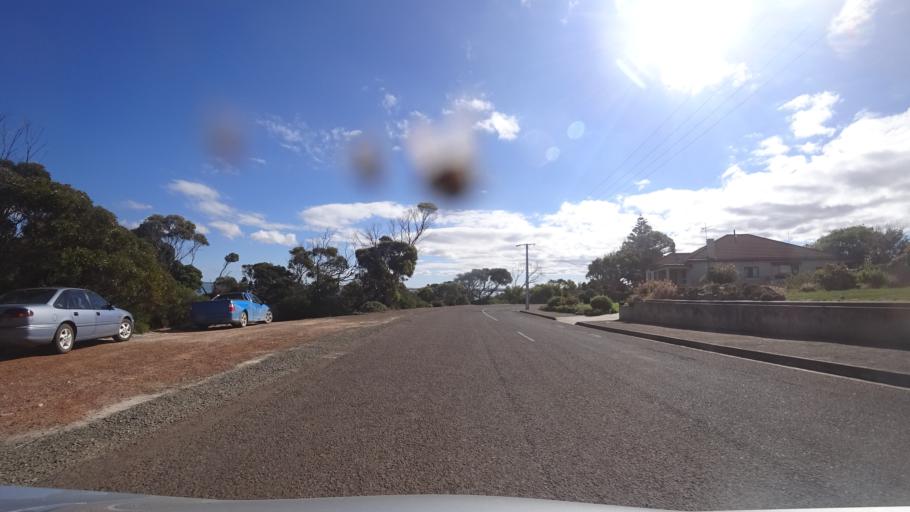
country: AU
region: South Australia
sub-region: Kangaroo Island
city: Kingscote
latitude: -35.6597
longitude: 137.6350
